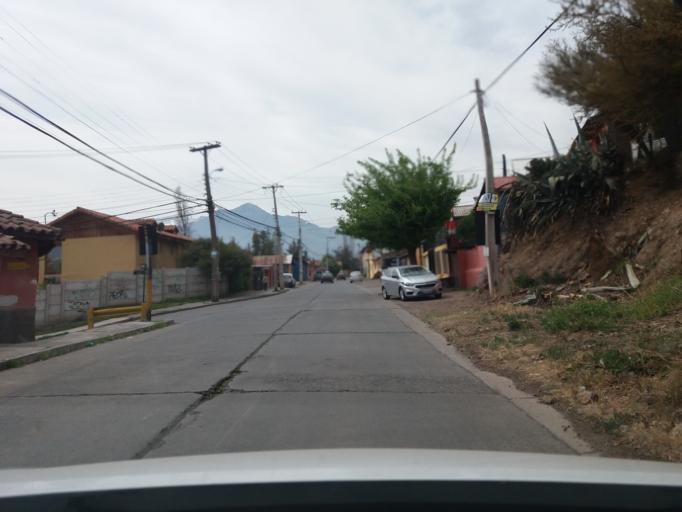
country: CL
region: Valparaiso
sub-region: Provincia de Los Andes
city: Los Andes
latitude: -32.8348
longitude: -70.5900
